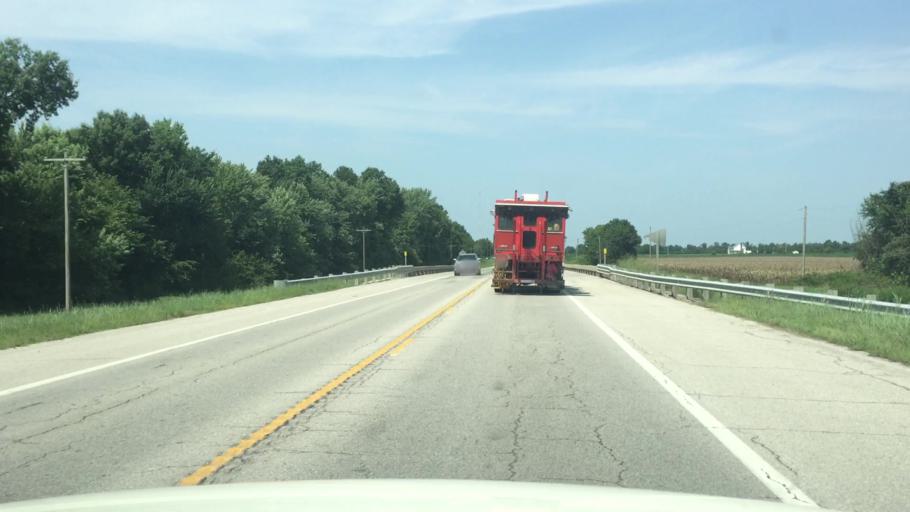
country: US
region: Kansas
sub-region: Cherokee County
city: Galena
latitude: 37.1820
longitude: -94.7045
